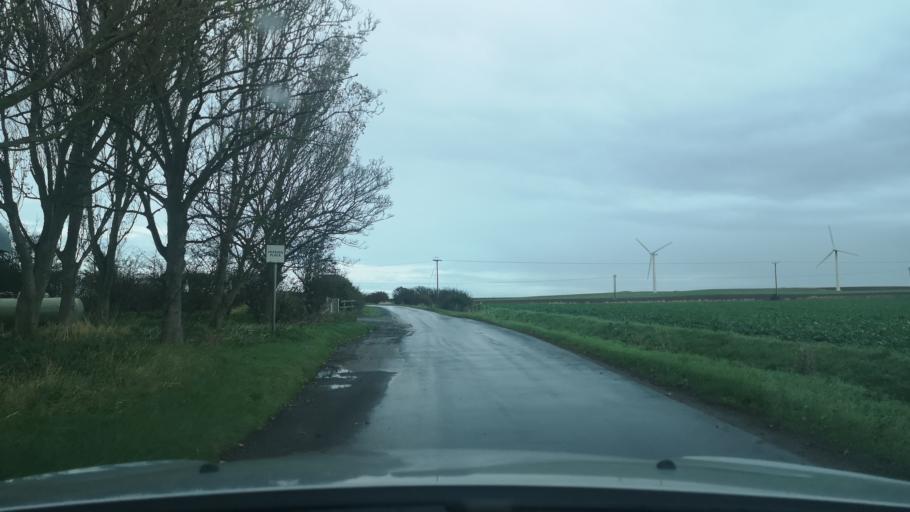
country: GB
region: England
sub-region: East Riding of Yorkshire
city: Easington
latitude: 53.6676
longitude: 0.0884
